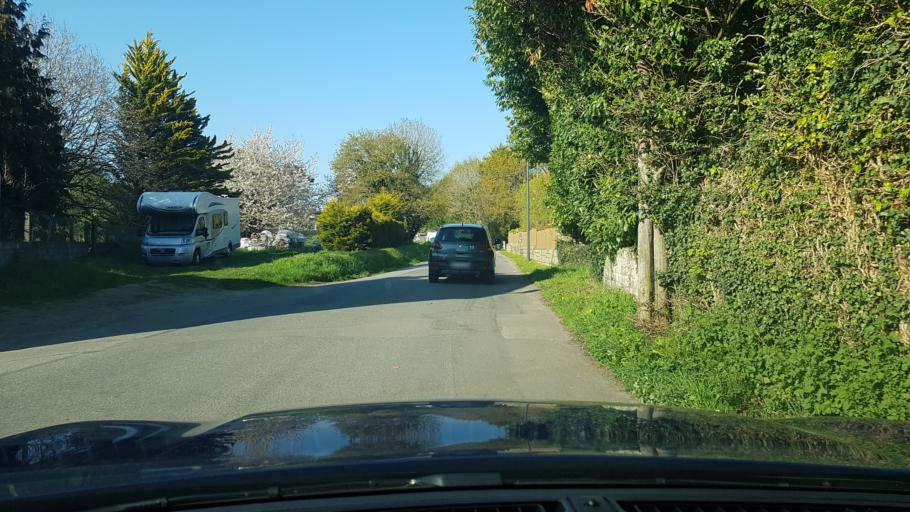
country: FR
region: Brittany
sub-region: Departement du Finistere
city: Moelan-sur-Mer
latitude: 47.7906
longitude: -3.6253
